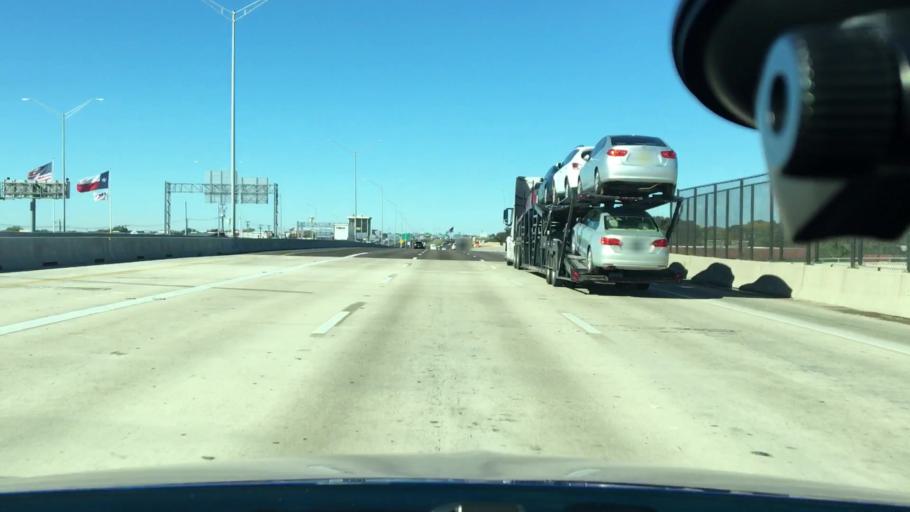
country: US
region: Texas
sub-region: Dallas County
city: Irving
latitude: 32.8375
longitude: -96.9387
